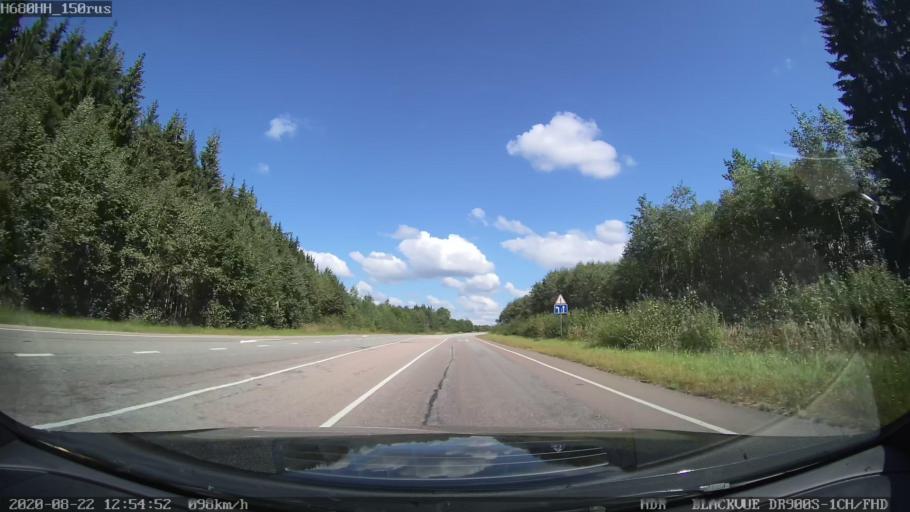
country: RU
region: Tverskaya
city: Rameshki
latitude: 57.5373
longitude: 36.2907
